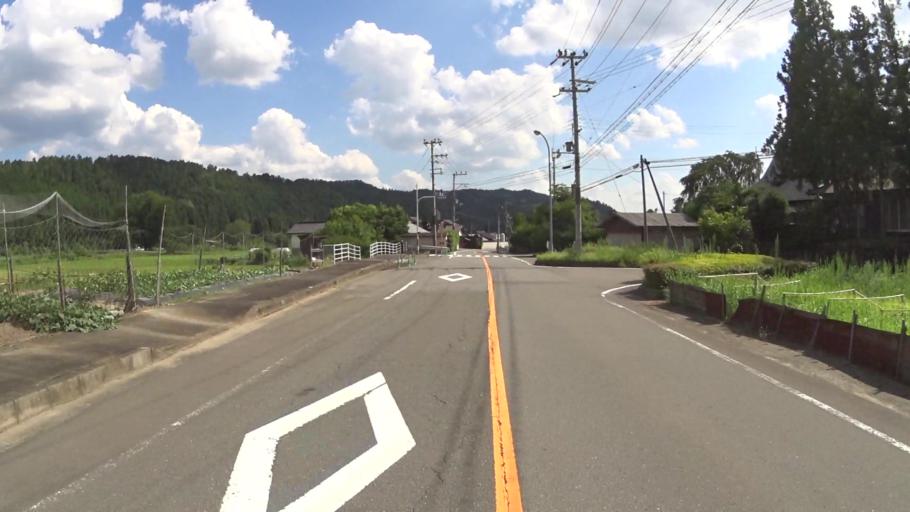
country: JP
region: Kyoto
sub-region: Kyoto-shi
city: Kamigyo-ku
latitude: 35.2035
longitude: 135.6407
